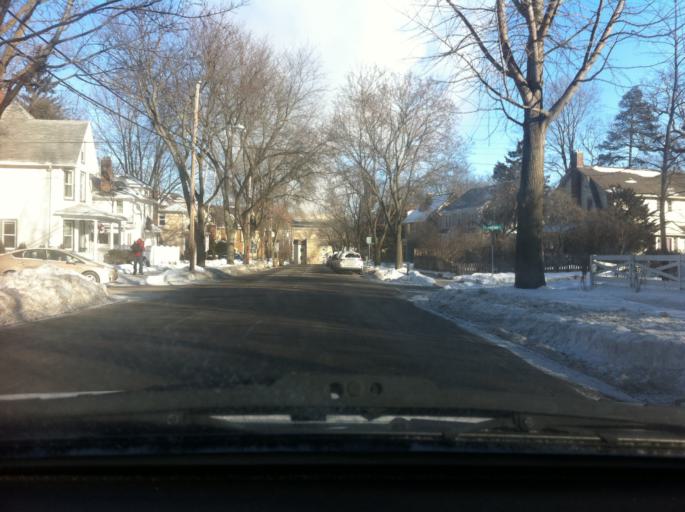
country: US
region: Wisconsin
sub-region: Dane County
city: Madison
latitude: 43.0705
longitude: -89.4239
